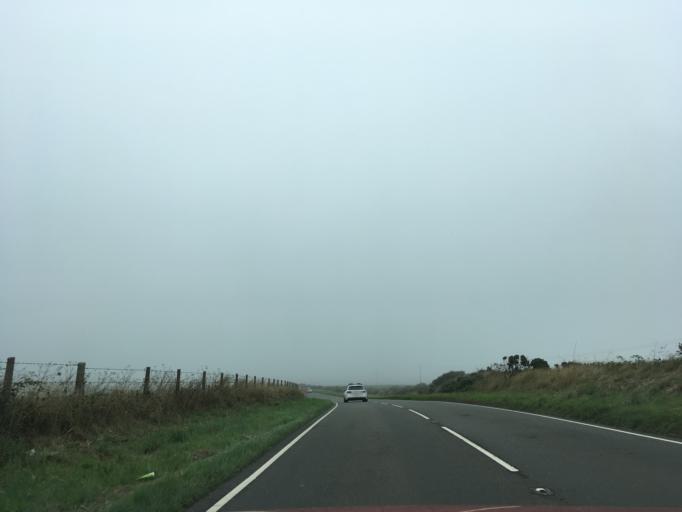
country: GB
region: Wales
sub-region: Pembrokeshire
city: Llanrhian
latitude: 51.8771
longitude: -5.1759
